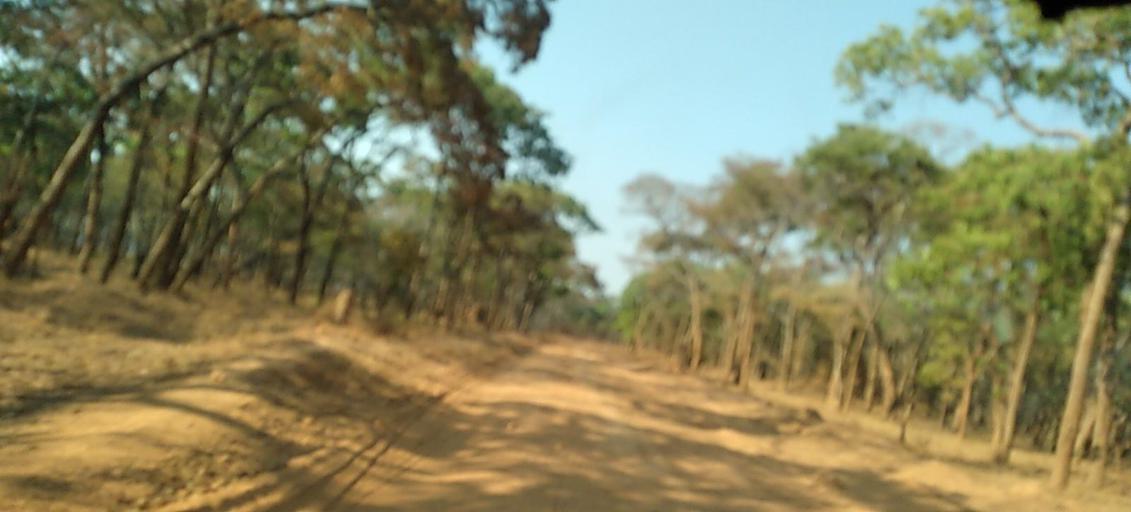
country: ZM
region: North-Western
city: Kasempa
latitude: -13.5997
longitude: 25.9796
